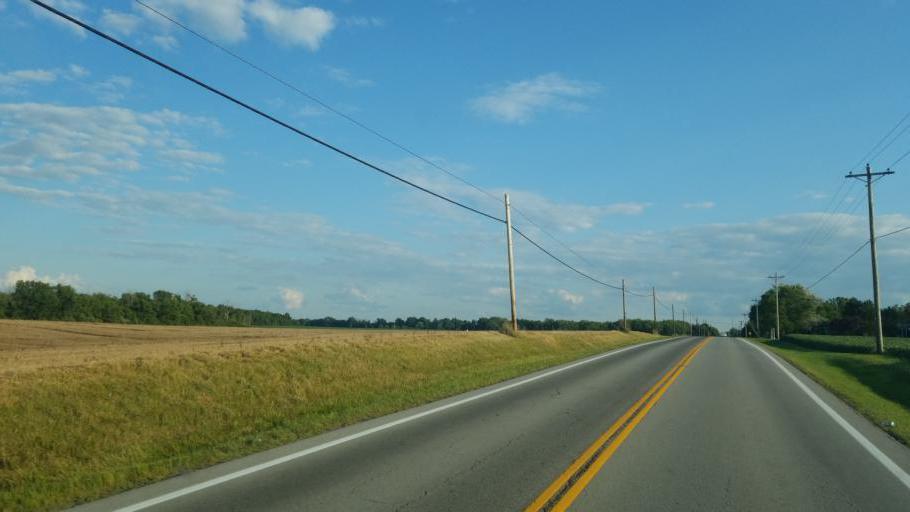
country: US
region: Ohio
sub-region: Huron County
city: Willard
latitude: 41.0886
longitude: -82.7183
